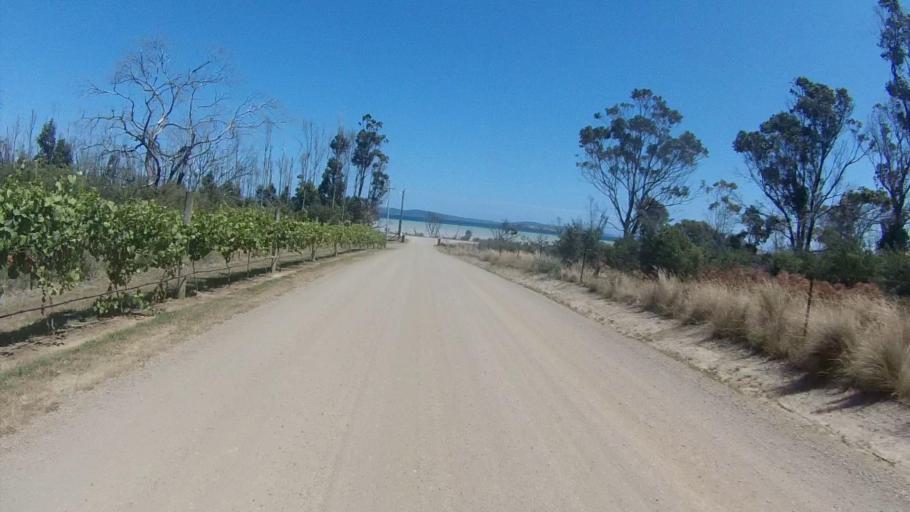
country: AU
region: Tasmania
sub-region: Sorell
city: Sorell
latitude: -42.8989
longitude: 147.8174
